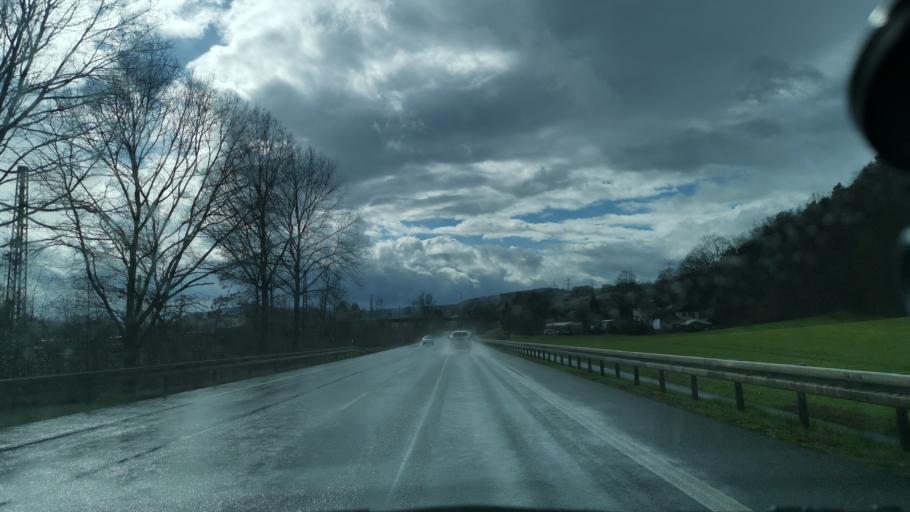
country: DE
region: Hesse
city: Breitenbach
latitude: 50.9256
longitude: 9.7641
